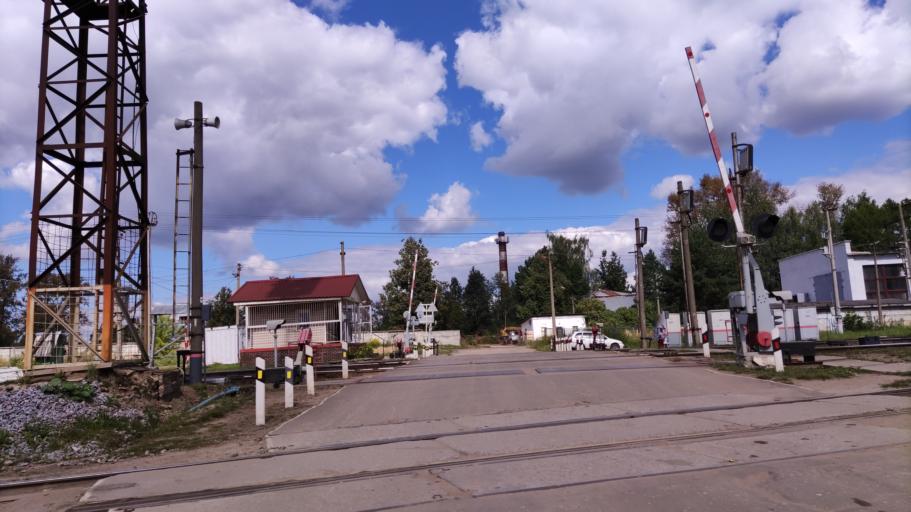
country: RU
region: Tverskaya
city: Rzhev
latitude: 56.2389
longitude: 34.3136
